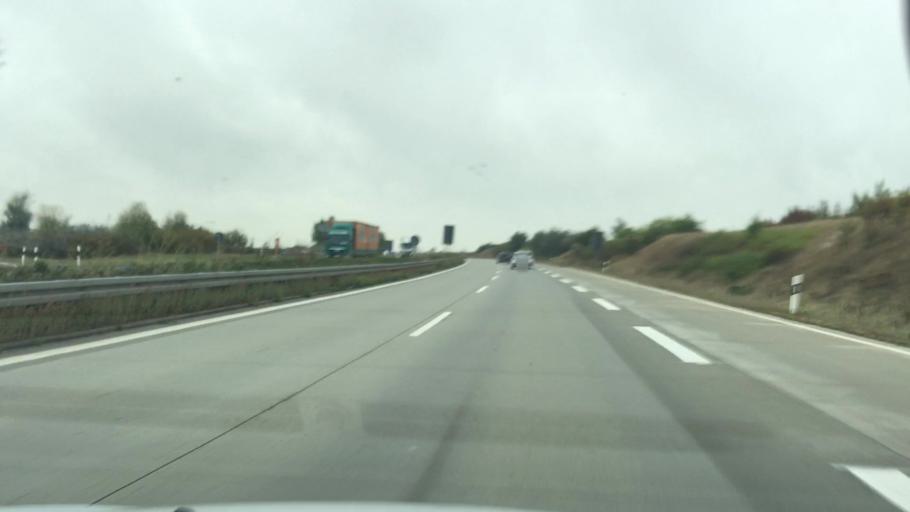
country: DE
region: Saxony
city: Niederfrohna
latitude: 50.9040
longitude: 12.7359
